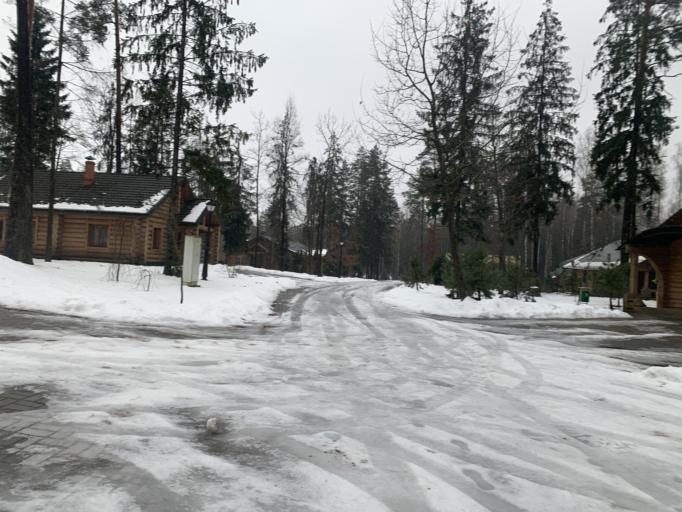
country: BY
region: Minsk
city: Slabada
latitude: 53.9484
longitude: 27.9838
